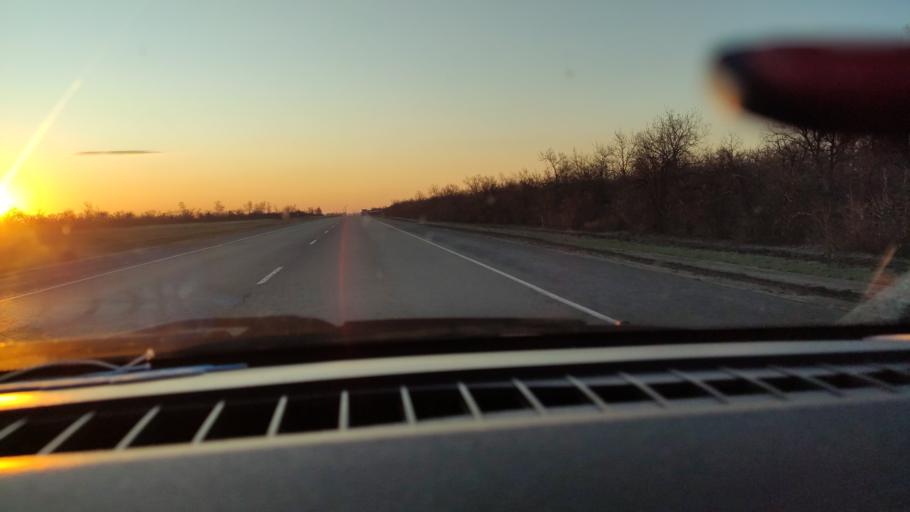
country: RU
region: Saratov
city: Yelshanka
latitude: 51.8209
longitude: 46.3407
